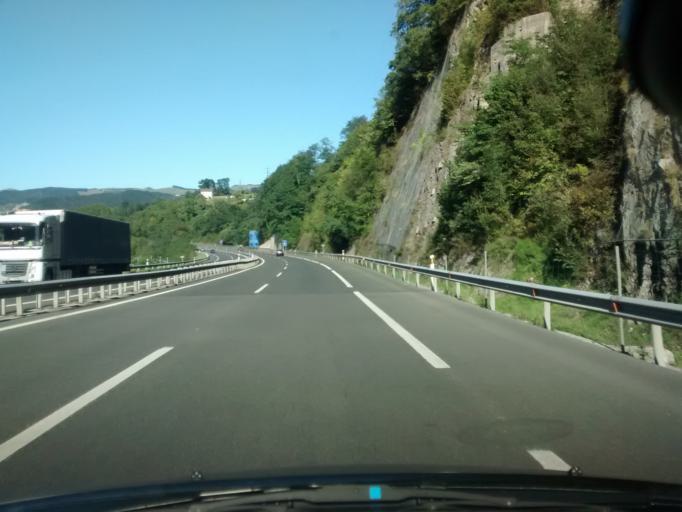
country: ES
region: Basque Country
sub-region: Provincia de Guipuzcoa
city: Elgoibar
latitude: 43.2032
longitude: -2.4259
